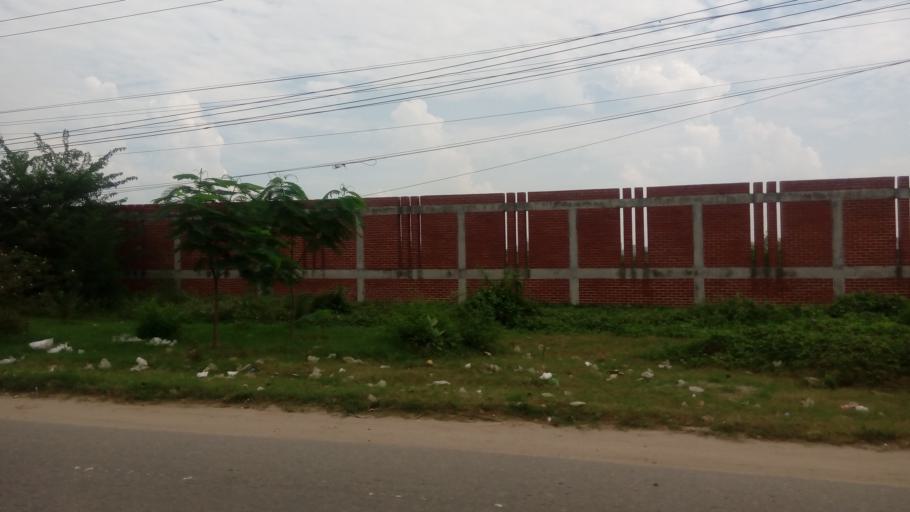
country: BD
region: Dhaka
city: Azimpur
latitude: 23.7491
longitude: 90.3533
